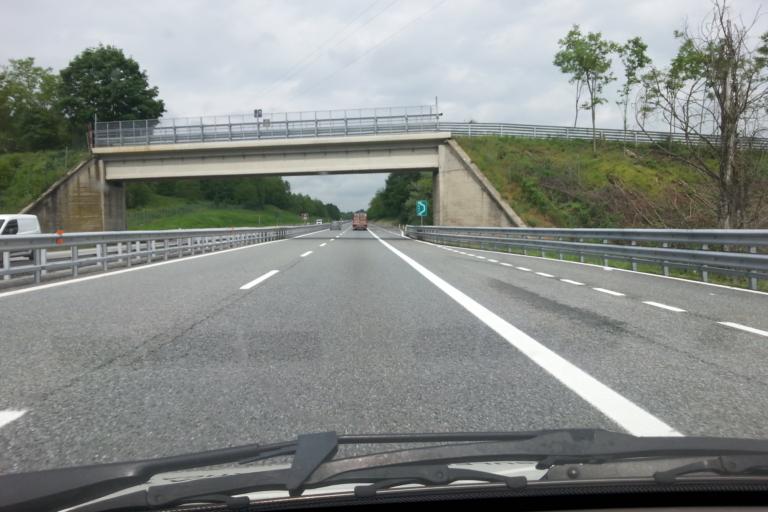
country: IT
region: Piedmont
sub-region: Provincia di Cuneo
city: Lesegno
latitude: 44.3935
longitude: 7.9905
